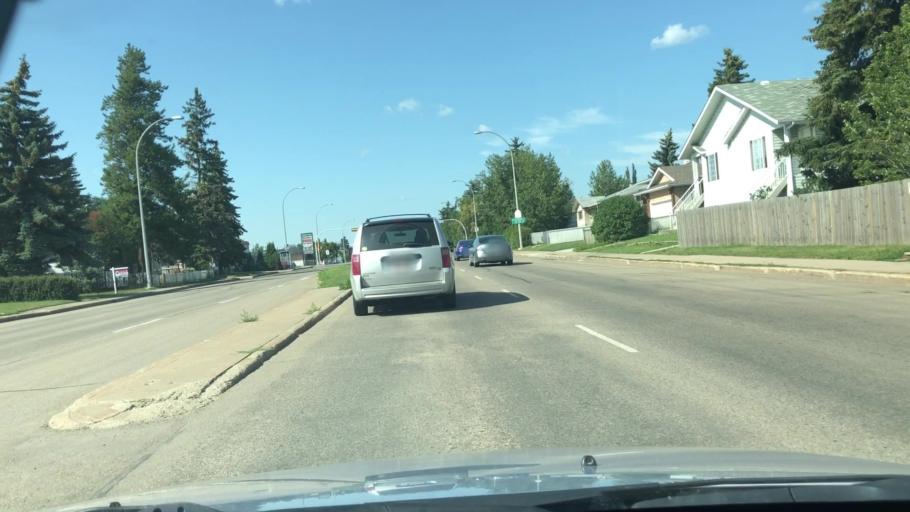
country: CA
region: Alberta
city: Edmonton
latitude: 53.5940
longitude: -113.4429
